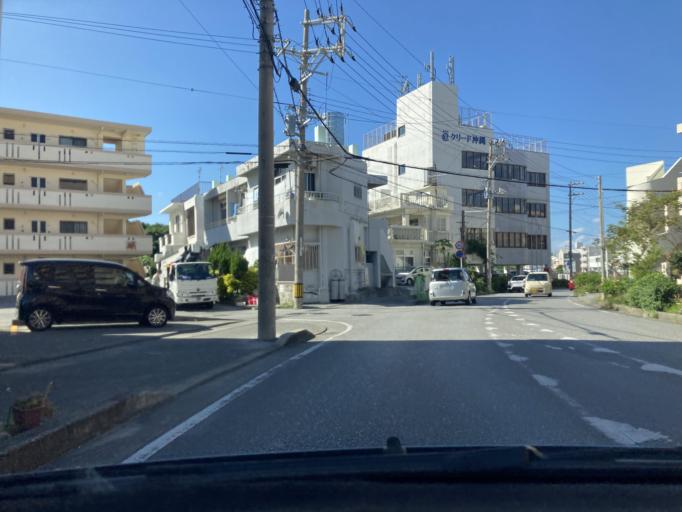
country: JP
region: Okinawa
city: Naha-shi
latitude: 26.2382
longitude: 127.6978
